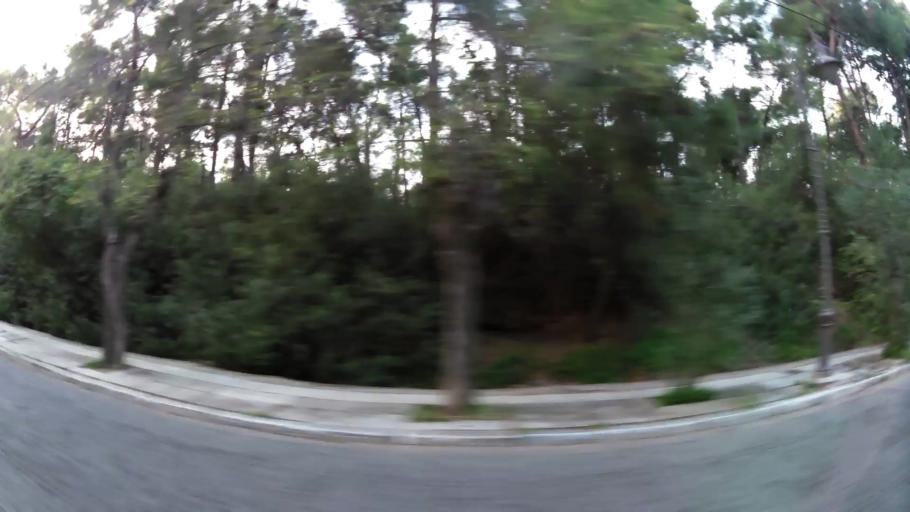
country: GR
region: Attica
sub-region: Nomarchia Athinas
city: Filothei
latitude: 38.0209
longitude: 23.7816
